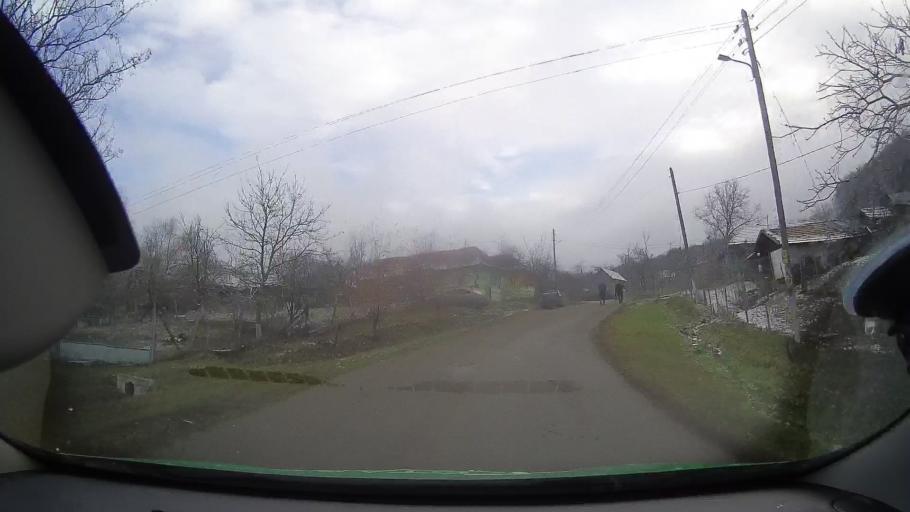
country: RO
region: Mures
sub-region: Comuna Chetani
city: Chetani
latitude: 46.4044
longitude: 24.0128
